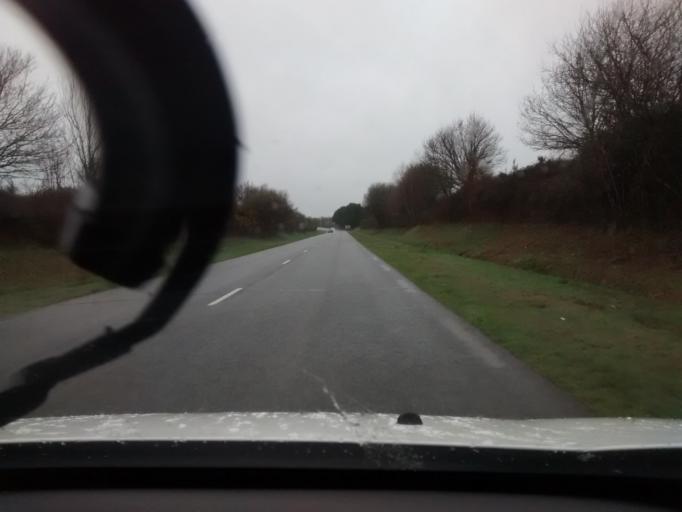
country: FR
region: Brittany
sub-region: Departement d'Ille-et-Vilaine
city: Acigne
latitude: 48.1274
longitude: -1.5260
